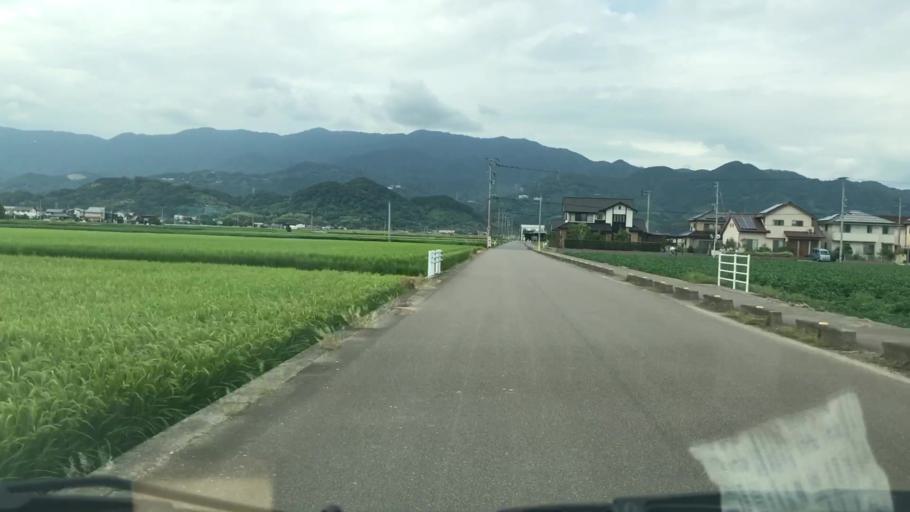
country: JP
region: Saga Prefecture
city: Saga-shi
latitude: 33.2846
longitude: 130.2256
